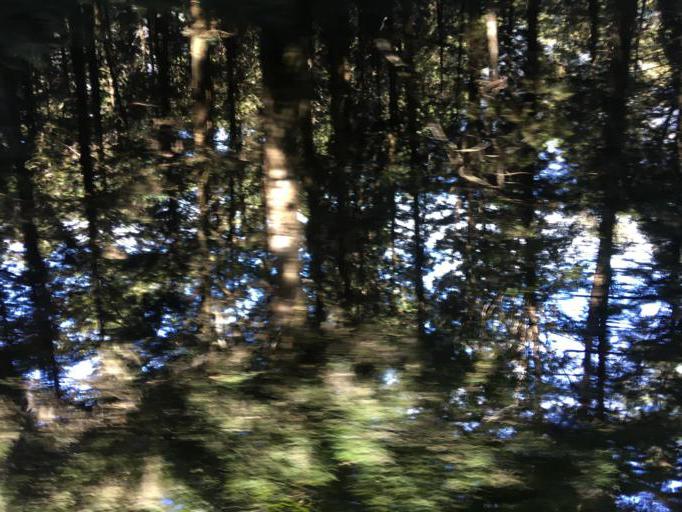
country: TW
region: Taiwan
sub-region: Yilan
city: Yilan
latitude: 24.5131
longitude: 121.5216
